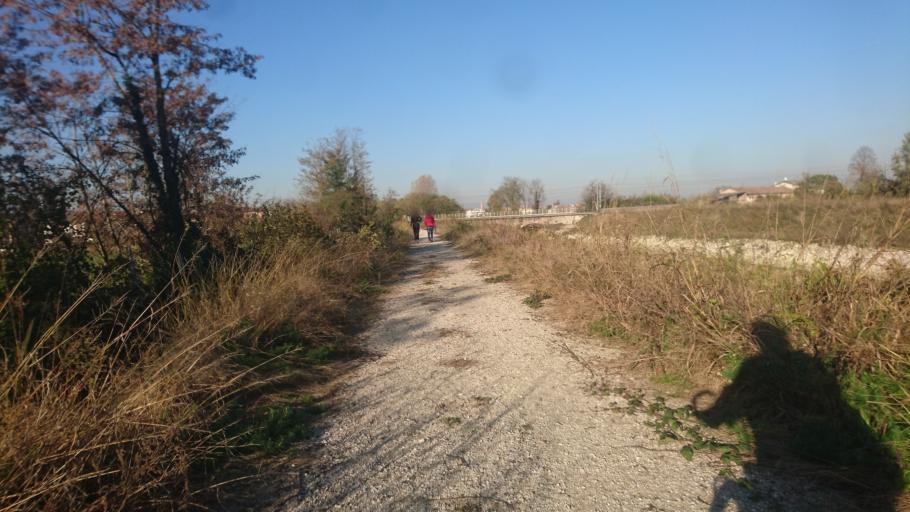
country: IT
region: Veneto
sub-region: Provincia di Padova
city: Villaguattera
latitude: 45.4370
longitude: 11.8282
